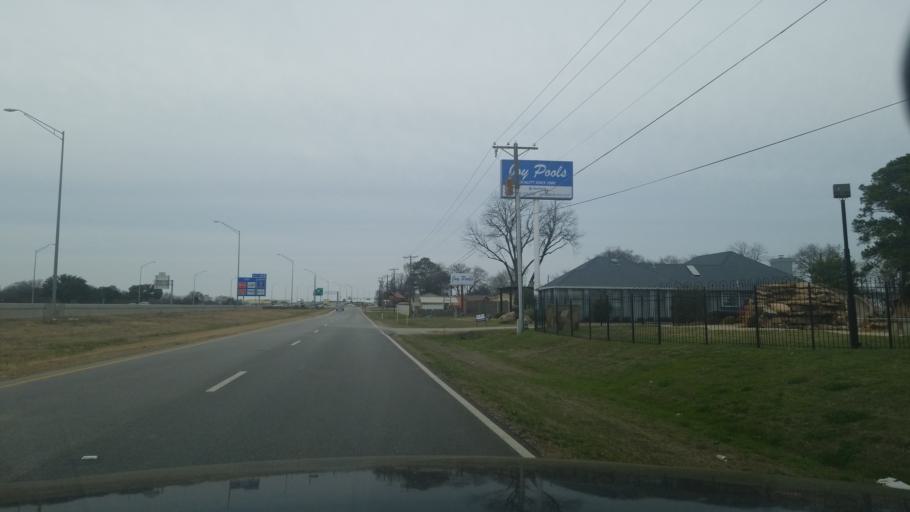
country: US
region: Texas
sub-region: Denton County
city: Lake Dallas
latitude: 33.1165
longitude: -97.0298
